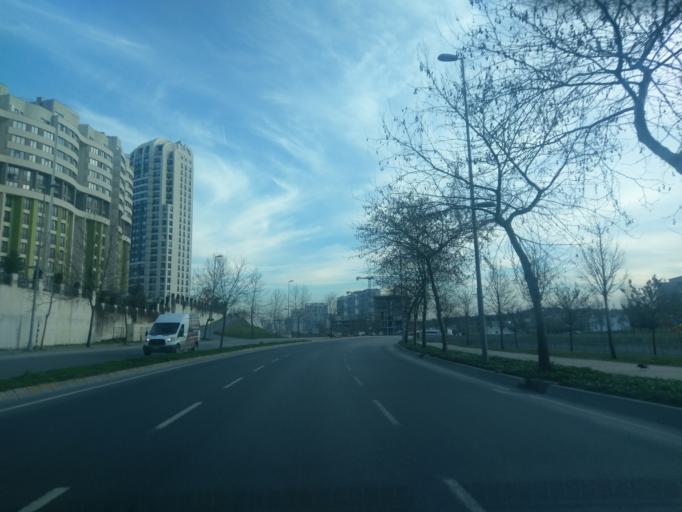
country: TR
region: Istanbul
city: Basaksehir
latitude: 41.0461
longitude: 28.7594
